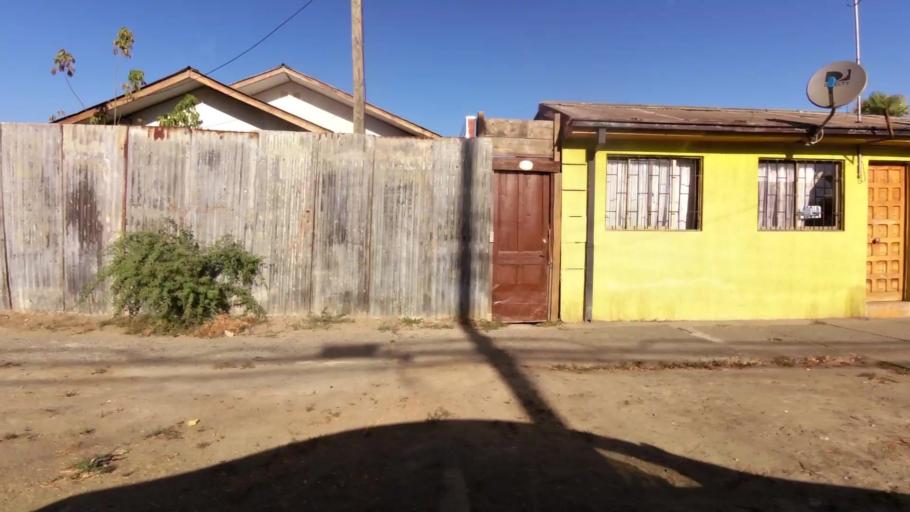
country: CL
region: Maule
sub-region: Provincia de Talca
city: Talca
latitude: -35.4359
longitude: -71.6543
